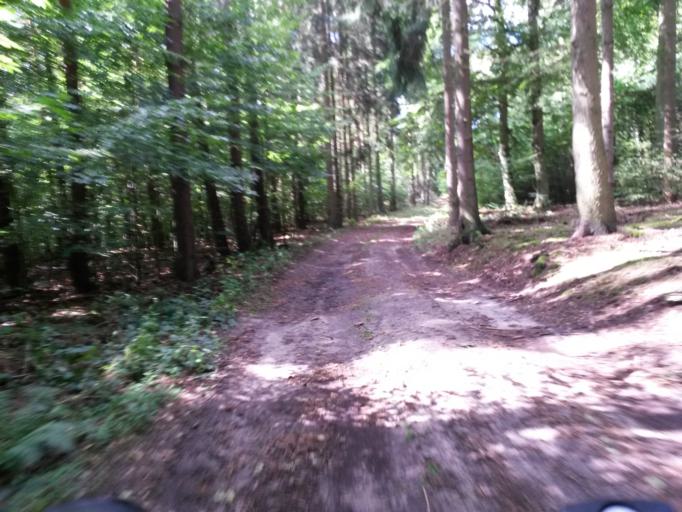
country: DE
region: Brandenburg
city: Milmersdorf
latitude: 53.1406
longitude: 13.6036
